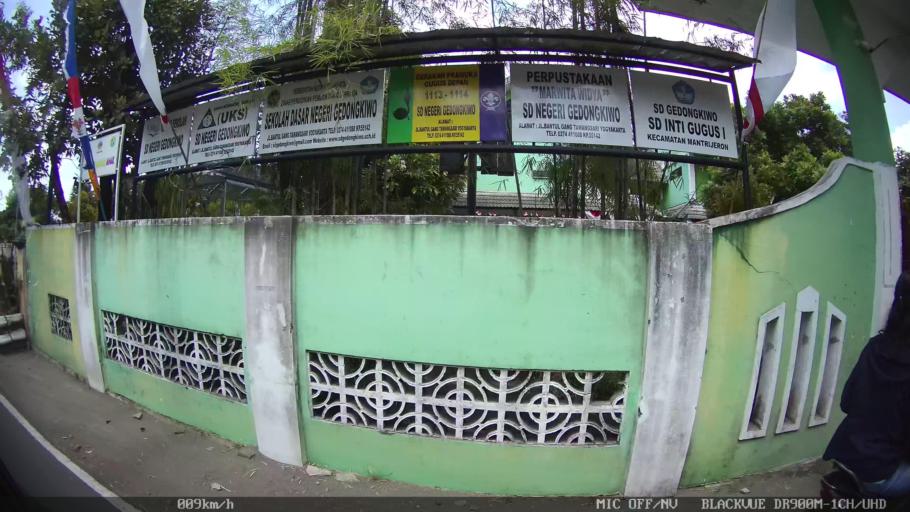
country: ID
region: Daerah Istimewa Yogyakarta
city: Kasihan
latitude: -7.8186
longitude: 110.3535
